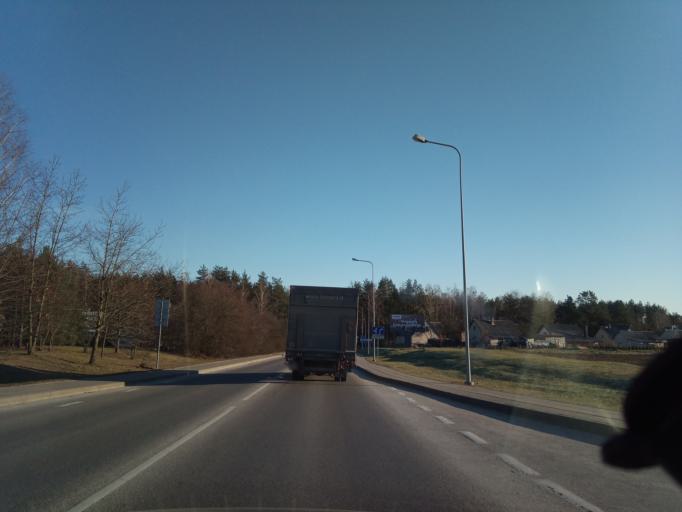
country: LT
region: Alytaus apskritis
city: Druskininkai
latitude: 54.0293
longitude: 23.9877
